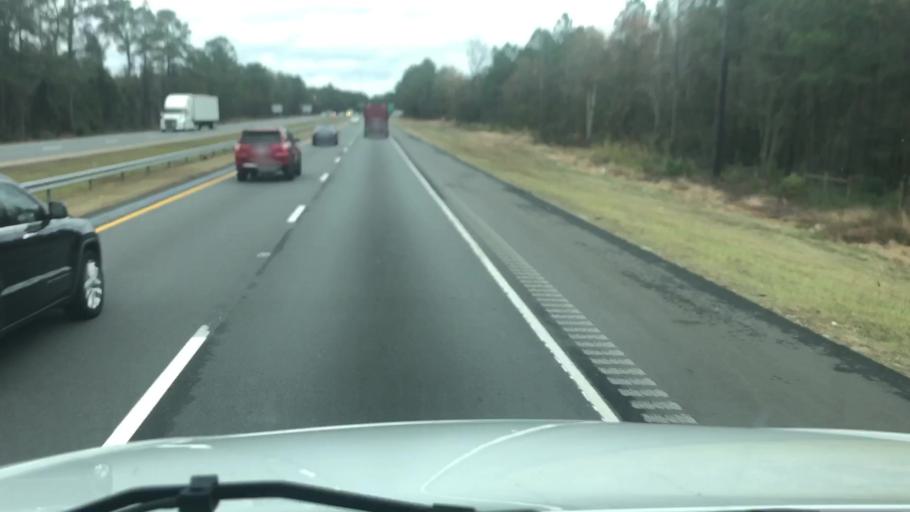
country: US
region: North Carolina
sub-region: Cumberland County
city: Eastover
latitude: 35.1060
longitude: -78.7703
